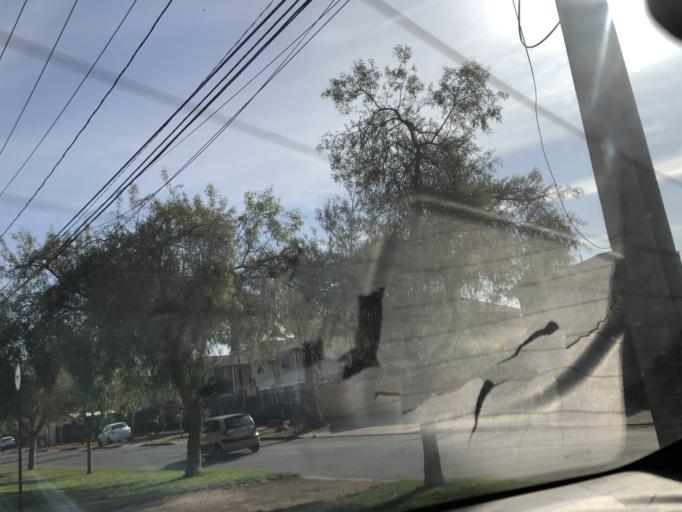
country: CL
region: Santiago Metropolitan
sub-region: Provincia de Cordillera
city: Puente Alto
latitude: -33.5988
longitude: -70.5822
